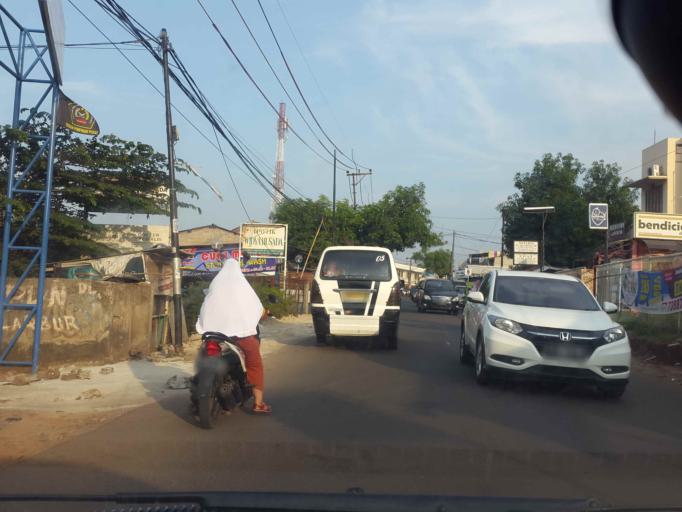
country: ID
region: Banten
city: South Tangerang
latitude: -6.2593
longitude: 106.7434
